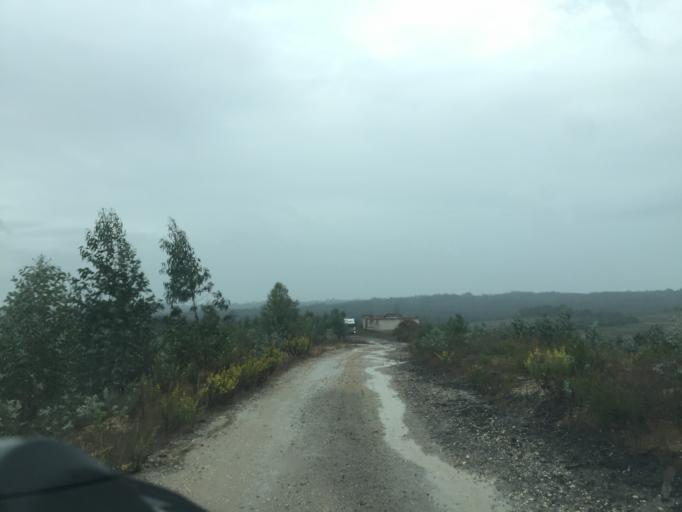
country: PT
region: Coimbra
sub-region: Figueira da Foz
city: Lavos
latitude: 40.0754
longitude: -8.7874
